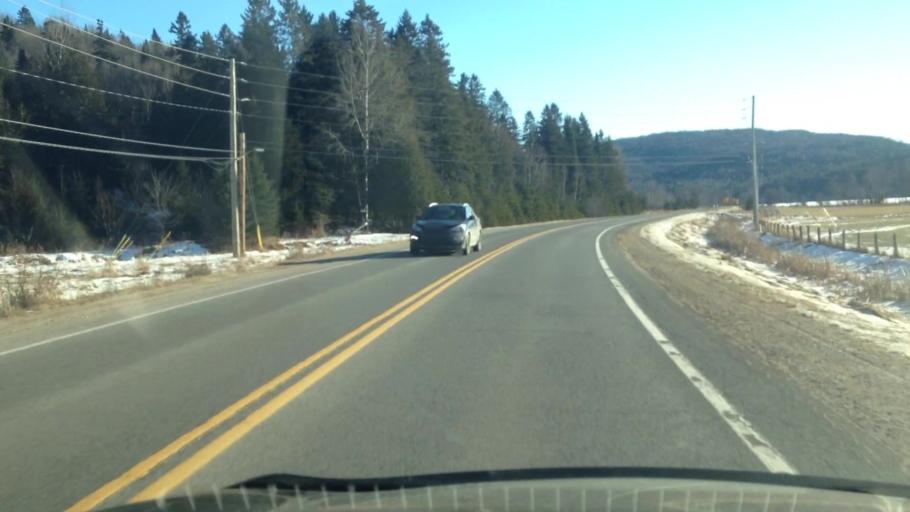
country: CA
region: Quebec
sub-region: Laurentides
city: Mont-Tremblant
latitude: 45.9563
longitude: -74.5666
